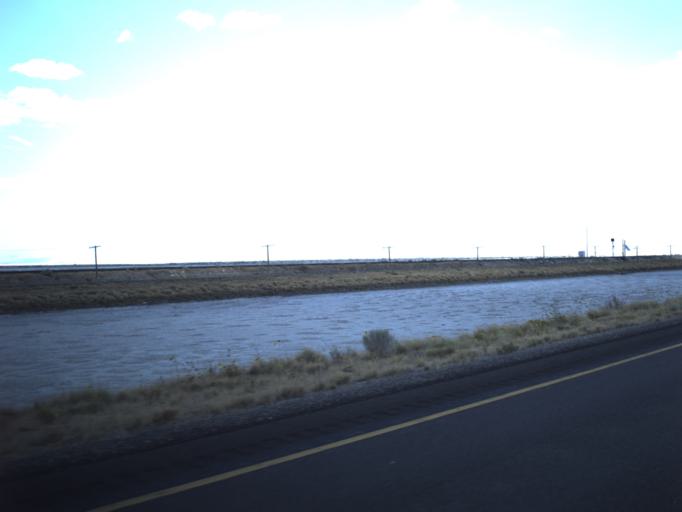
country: US
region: Utah
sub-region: Tooele County
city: Grantsville
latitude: 40.7266
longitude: -112.5777
